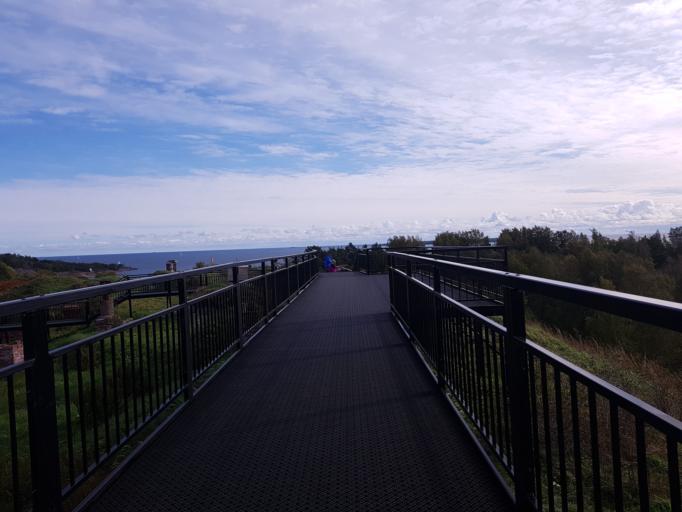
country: FI
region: Uusimaa
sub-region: Helsinki
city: Helsinki
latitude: 60.1347
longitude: 24.9989
